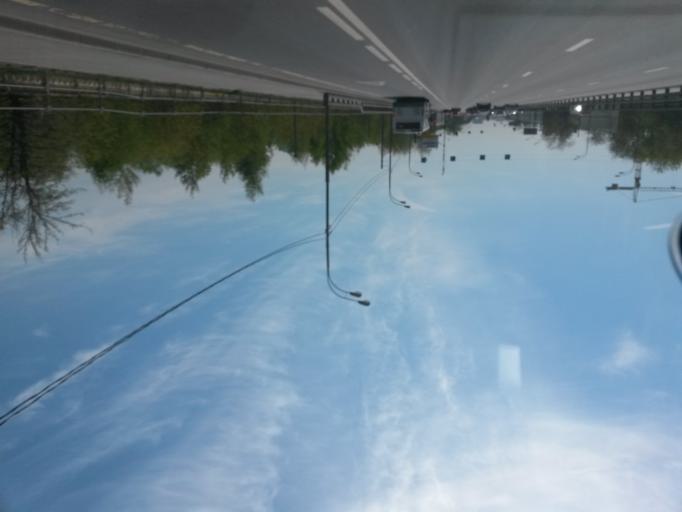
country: RU
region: Moscow
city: Annino
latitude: 55.5477
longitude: 37.5857
